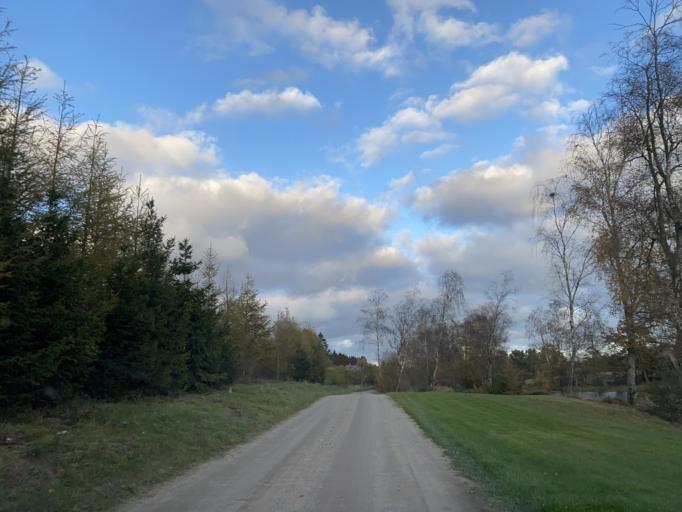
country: DK
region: Central Jutland
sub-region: Silkeborg Kommune
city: Svejbaek
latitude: 56.1792
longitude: 9.6191
